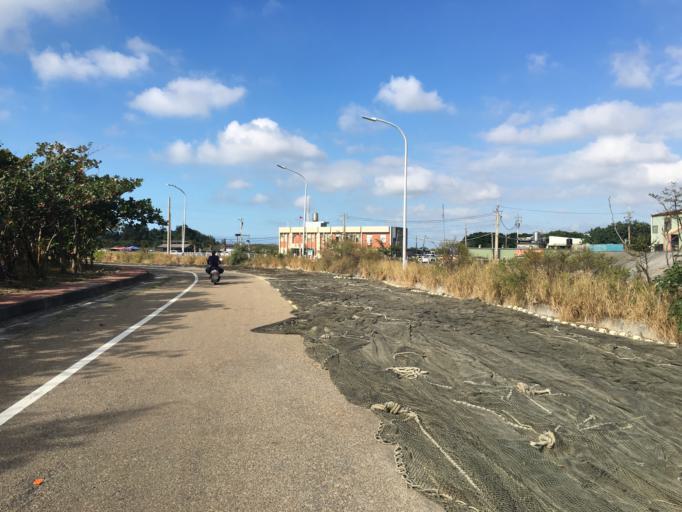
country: TW
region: Taiwan
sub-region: Hsinchu
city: Hsinchu
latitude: 24.7628
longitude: 120.9056
